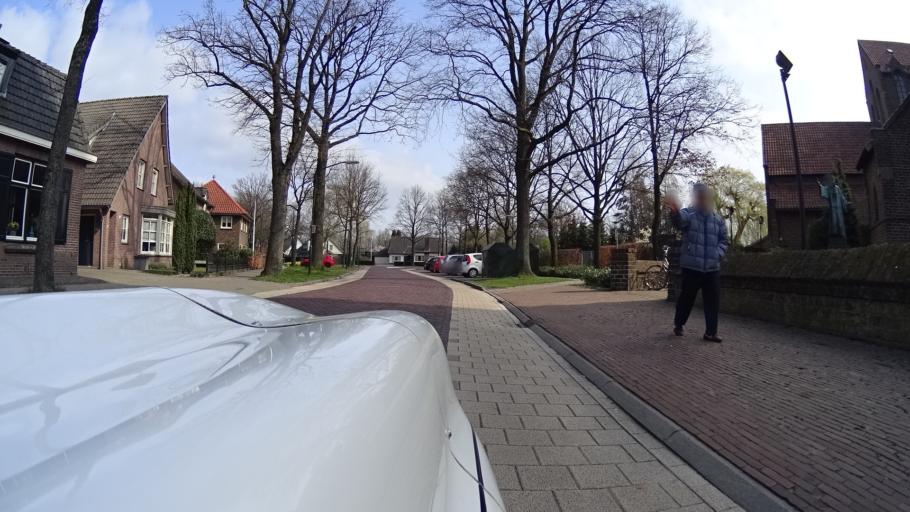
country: NL
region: North Brabant
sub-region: Gemeente Laarbeek
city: Aarle-Rixtel
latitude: 51.5295
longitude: 5.6355
